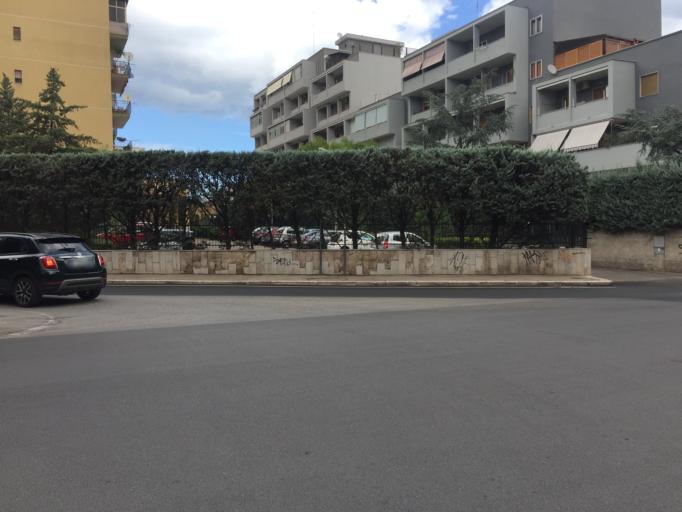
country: IT
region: Apulia
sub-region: Provincia di Bari
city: Bari
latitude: 41.0931
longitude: 16.8624
